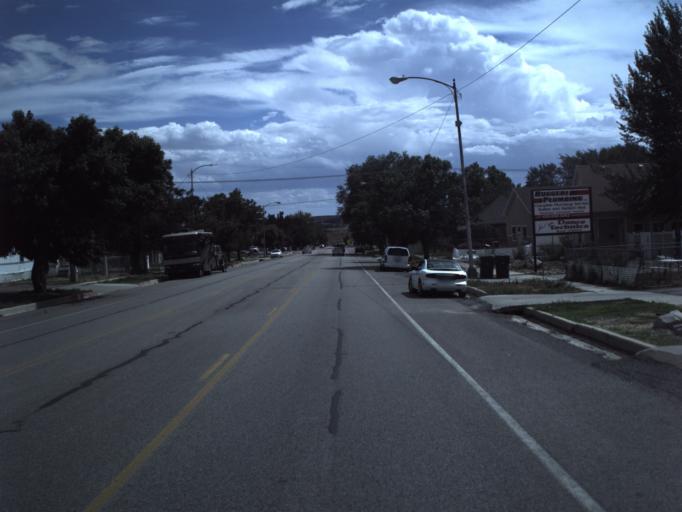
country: US
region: Utah
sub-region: Carbon County
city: Price
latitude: 39.5961
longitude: -110.8113
